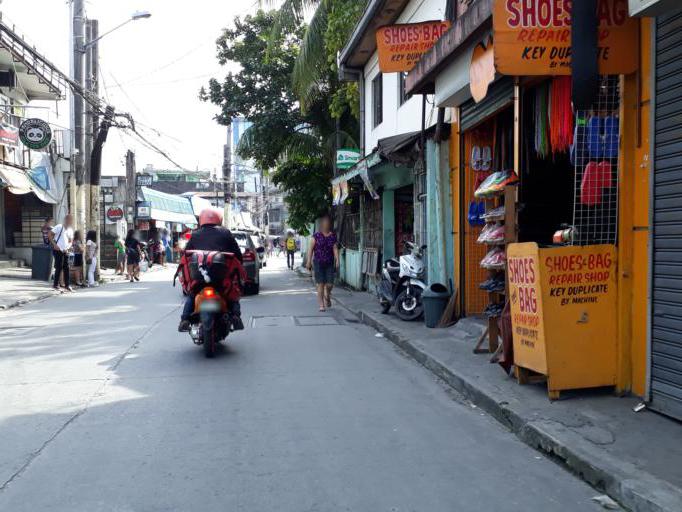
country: PH
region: Calabarzon
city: Bagong Pagasa
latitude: 14.6764
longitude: 121.0046
